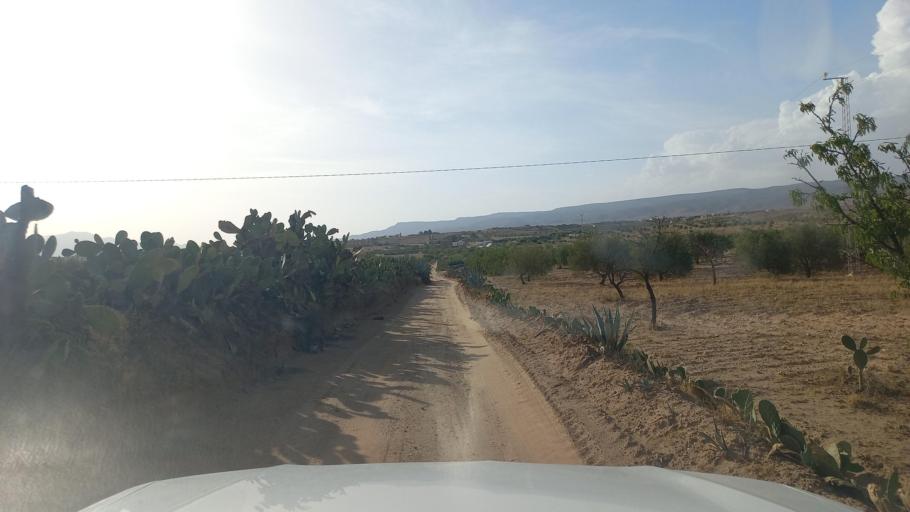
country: TN
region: Al Qasrayn
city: Kasserine
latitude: 35.2358
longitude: 8.9172
